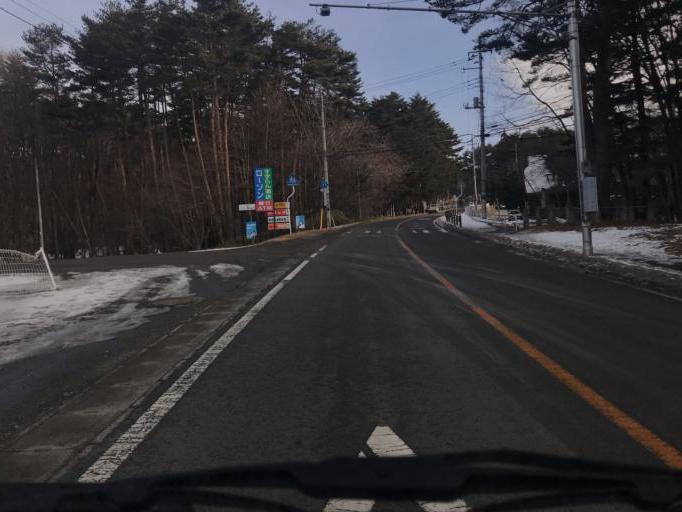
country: JP
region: Nagano
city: Chino
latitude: 35.8768
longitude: 138.3126
